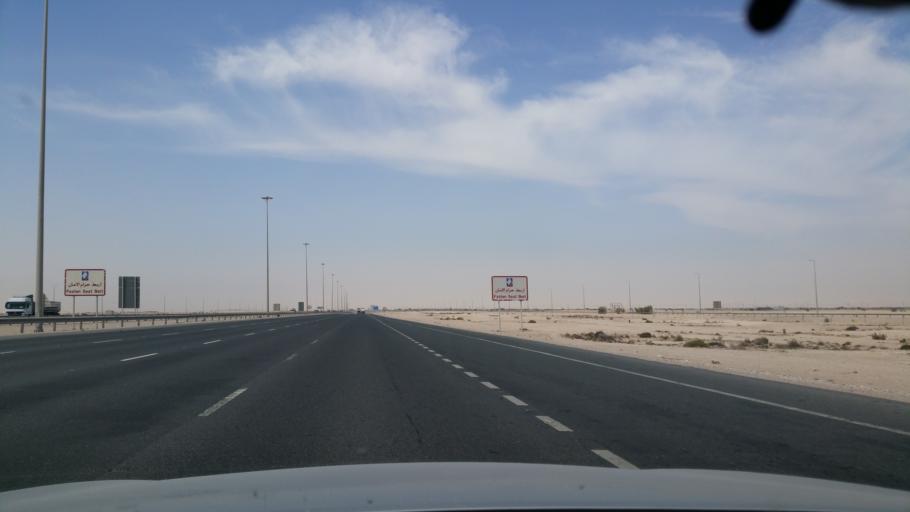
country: QA
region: Baladiyat ar Rayyan
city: Ash Shahaniyah
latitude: 25.1040
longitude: 51.1586
